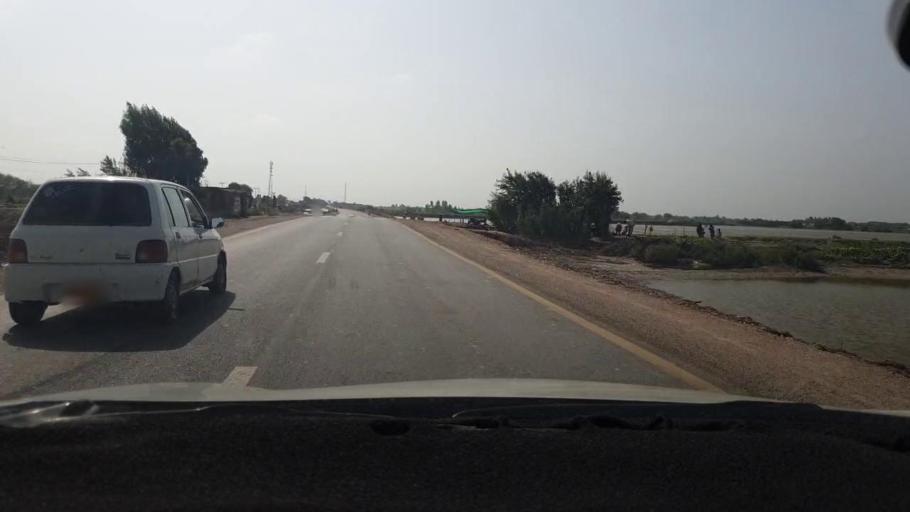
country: PK
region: Sindh
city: Jhol
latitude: 25.8908
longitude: 69.0300
